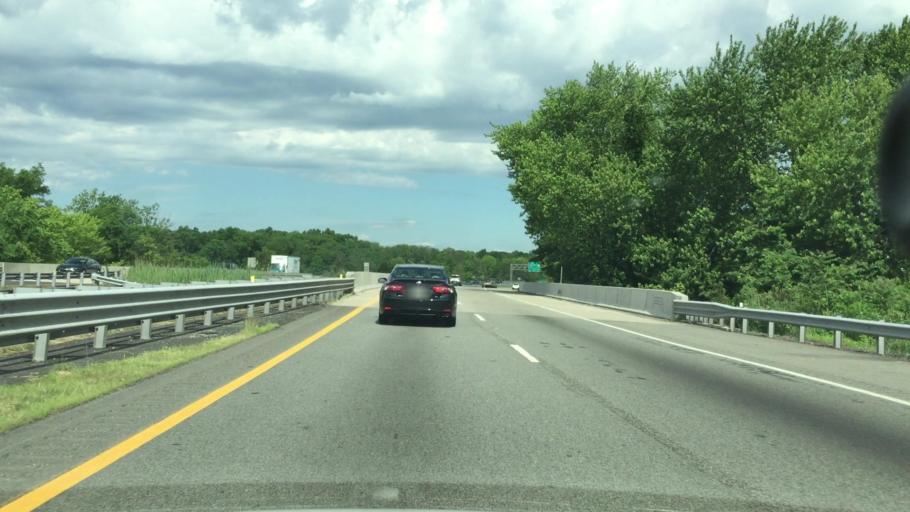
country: US
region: New Jersey
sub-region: Morris County
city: East Hanover
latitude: 40.8447
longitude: -74.3474
